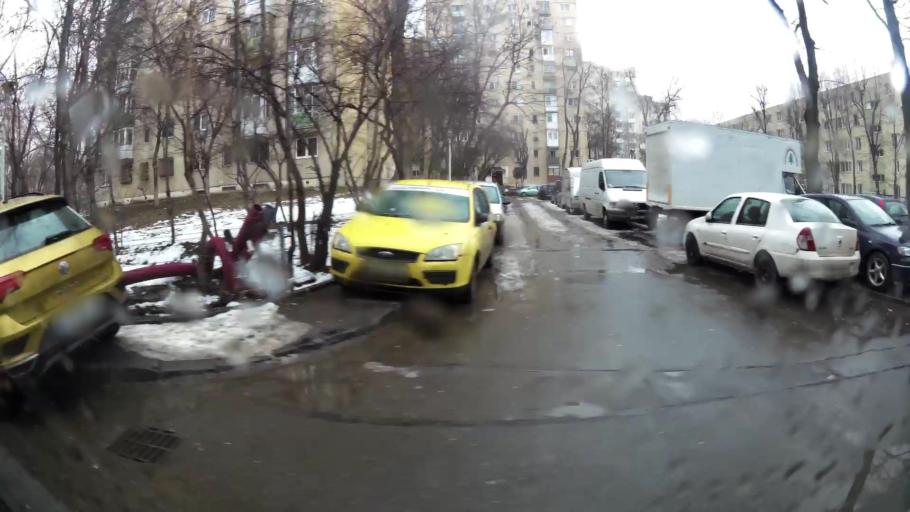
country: RO
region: Ilfov
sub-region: Comuna Chiajna
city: Rosu
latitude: 44.4155
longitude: 26.0219
